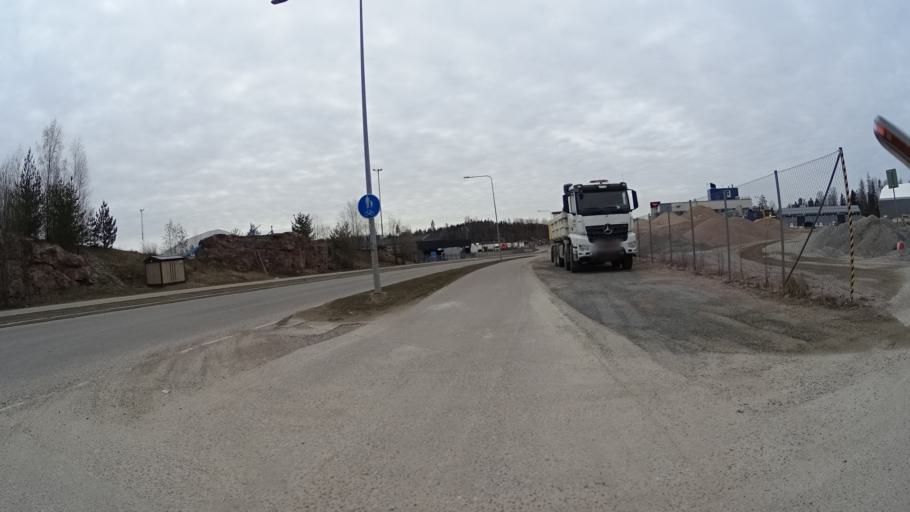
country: FI
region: Uusimaa
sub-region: Helsinki
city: Teekkarikylae
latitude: 60.3020
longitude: 24.9065
